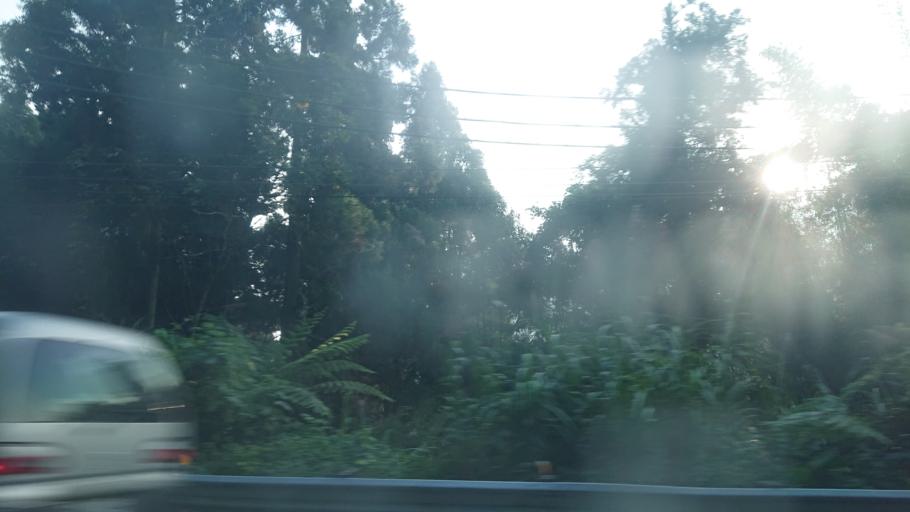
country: TW
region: Taiwan
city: Lugu
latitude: 23.4867
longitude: 120.7500
